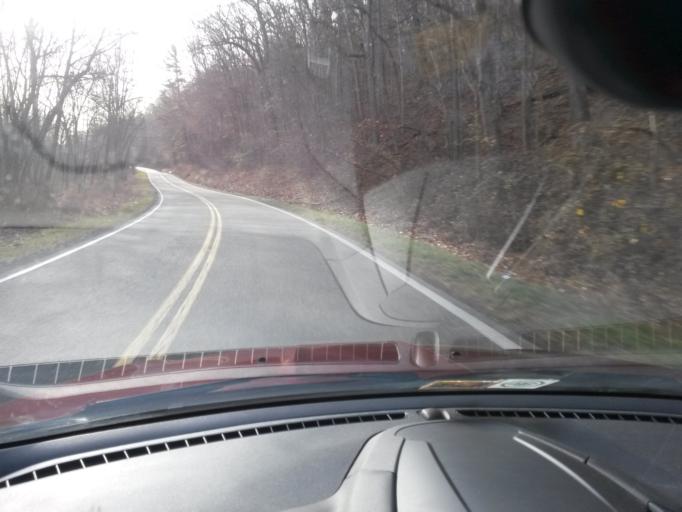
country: US
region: Virginia
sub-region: Bath County
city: Warm Springs
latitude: 38.0089
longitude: -79.5467
